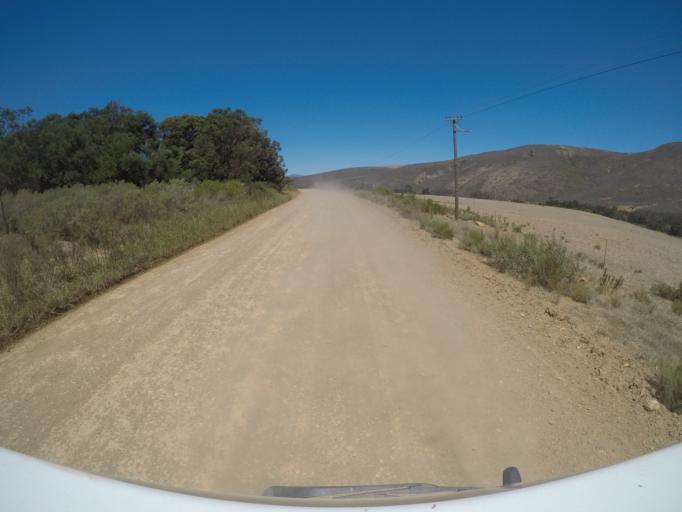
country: ZA
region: Western Cape
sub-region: Overberg District Municipality
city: Caledon
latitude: -34.1263
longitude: 19.2387
